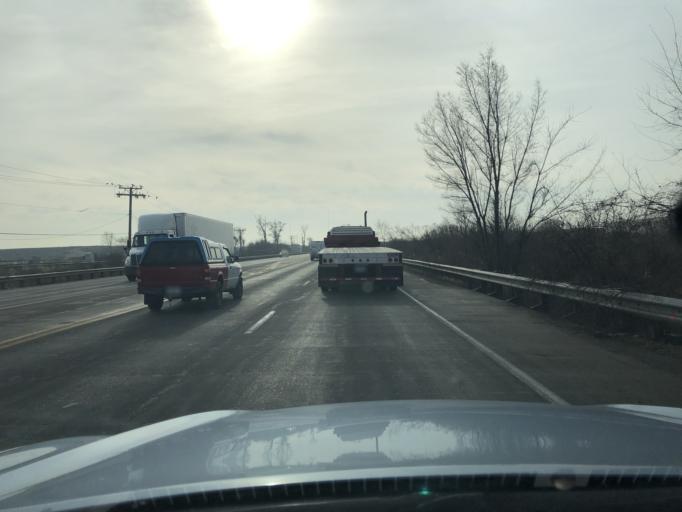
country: US
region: Illinois
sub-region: DuPage County
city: Bensenville
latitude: 41.9870
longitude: -87.9399
